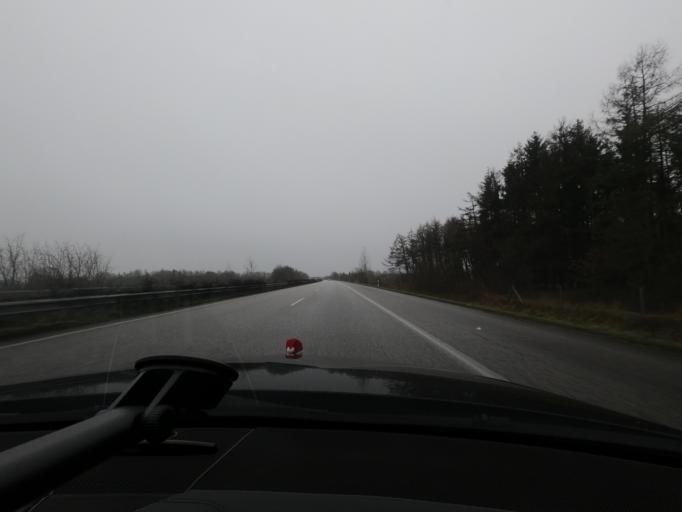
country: DE
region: Schleswig-Holstein
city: Bollingstedt
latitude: 54.6103
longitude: 9.4459
